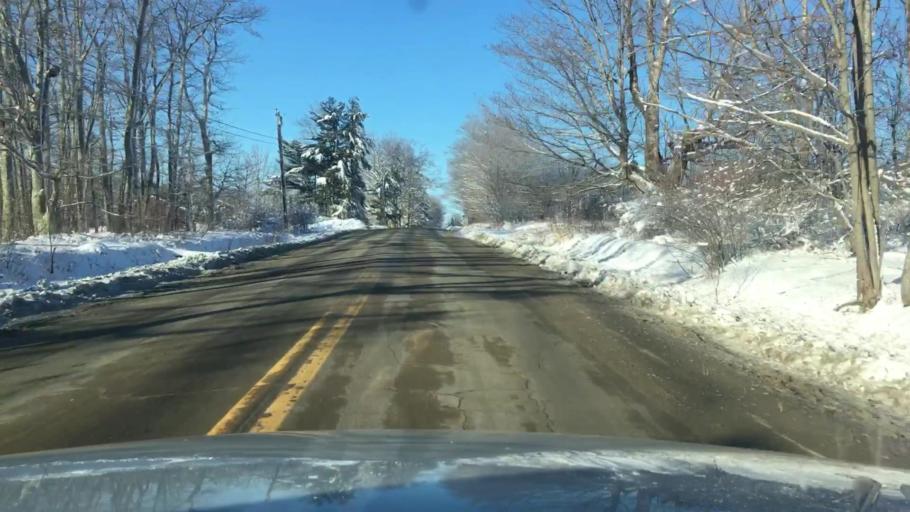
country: US
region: Maine
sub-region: Kennebec County
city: Readfield
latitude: 44.4304
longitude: -69.9413
